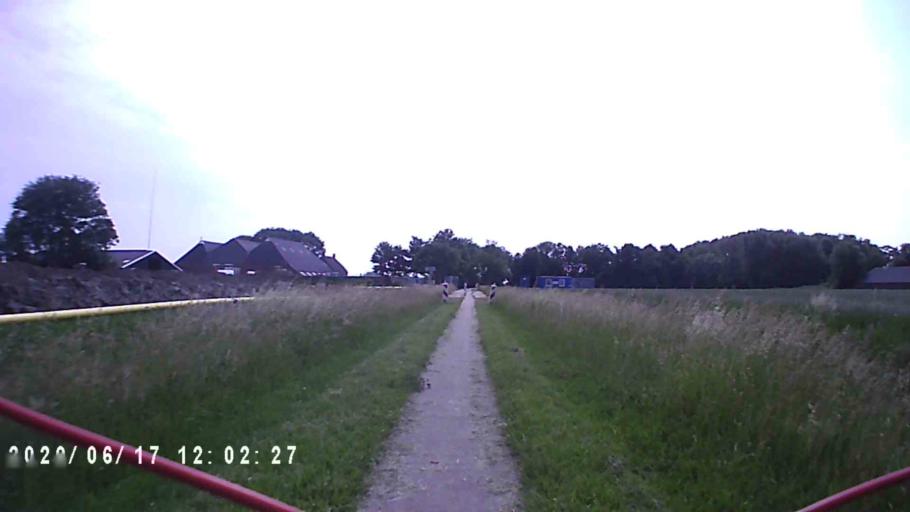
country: NL
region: Groningen
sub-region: Gemeente De Marne
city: Ulrum
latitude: 53.3400
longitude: 6.3404
